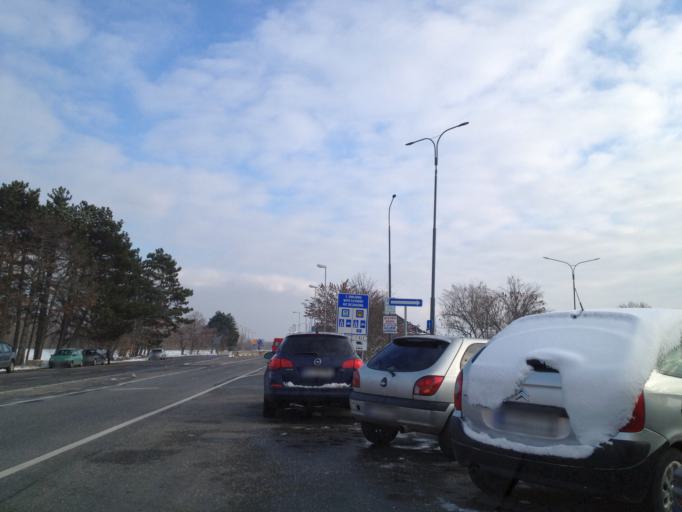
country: AT
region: Burgenland
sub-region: Politischer Bezirk Neusiedl am See
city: Kittsee
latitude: 48.1220
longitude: 17.0628
